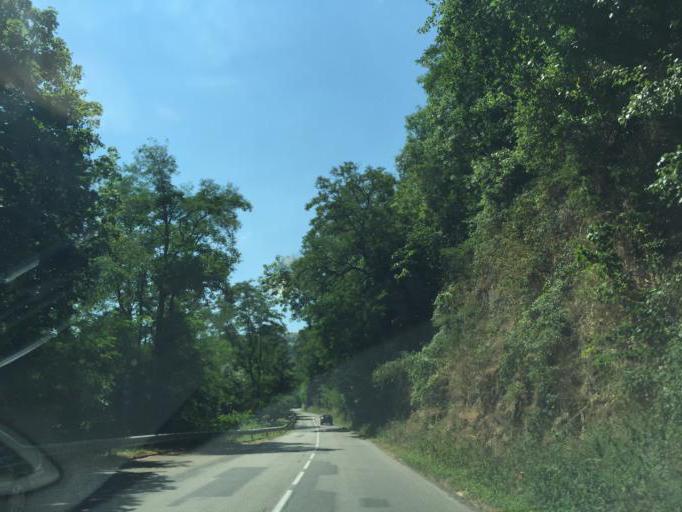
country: FR
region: Rhone-Alpes
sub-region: Departement de la Loire
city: Saint-Chamond
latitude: 45.4356
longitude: 4.5112
